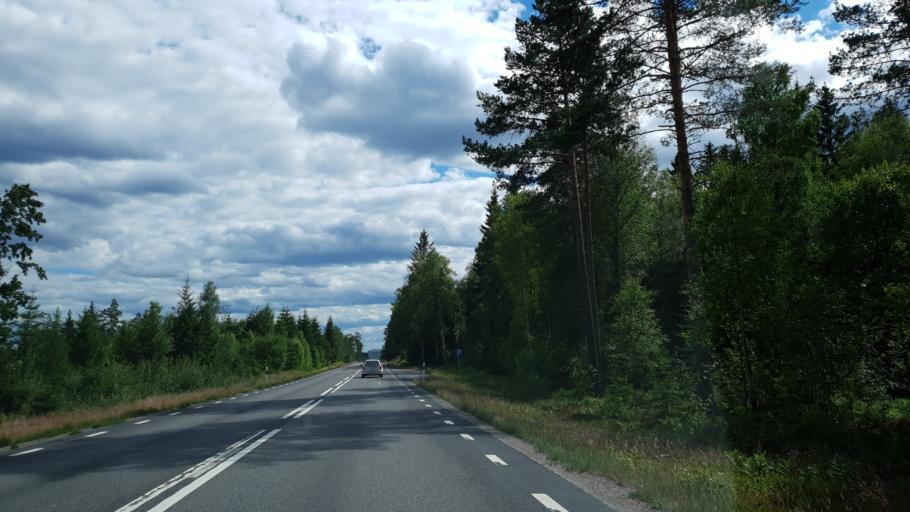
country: SE
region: Kronoberg
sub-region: Lessebo Kommun
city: Lessebo
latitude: 56.8149
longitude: 15.4113
